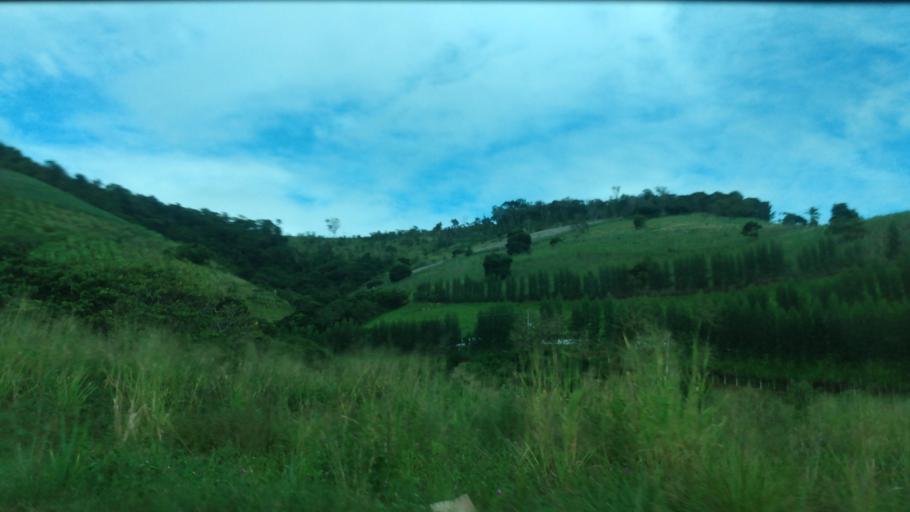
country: BR
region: Pernambuco
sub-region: Maraial
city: Maraial
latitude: -8.7214
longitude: -35.7829
